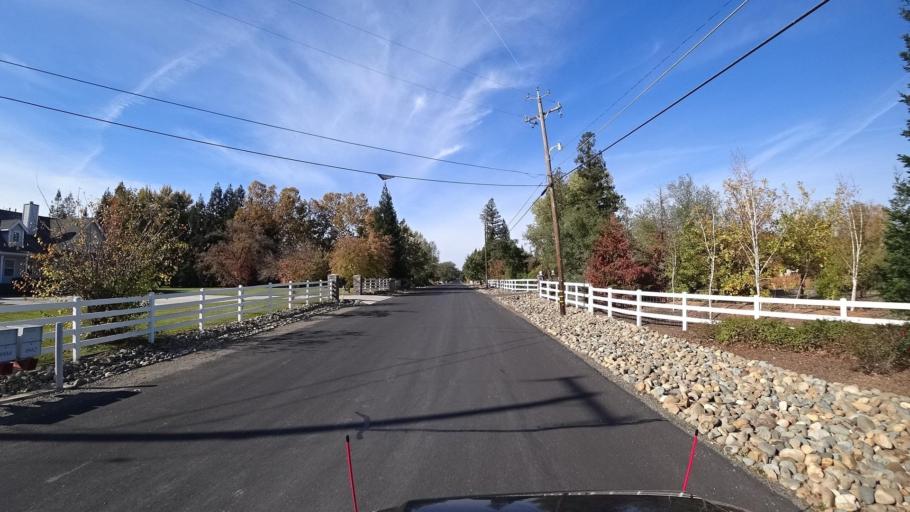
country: US
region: California
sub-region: Sacramento County
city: Wilton
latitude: 38.4292
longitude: -121.2877
